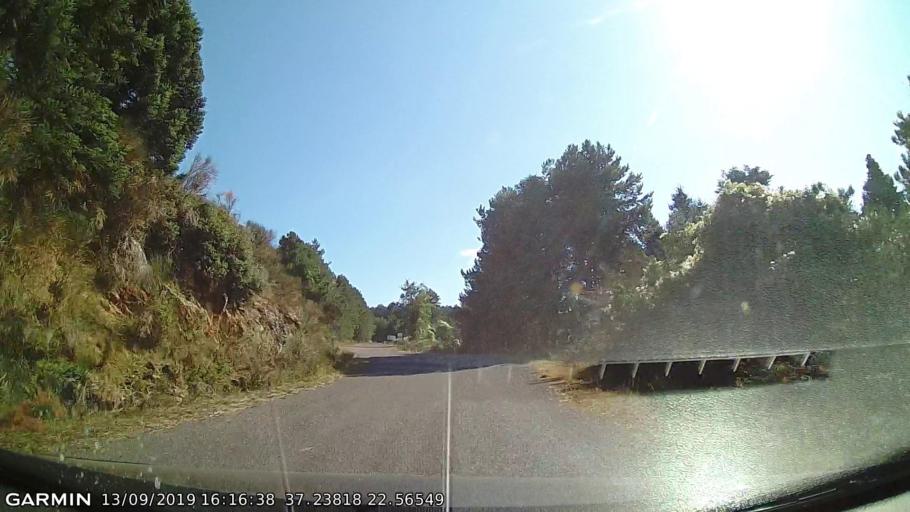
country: GR
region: Peloponnese
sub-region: Nomos Lakonias
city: Kariai
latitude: 37.2380
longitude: 22.5654
